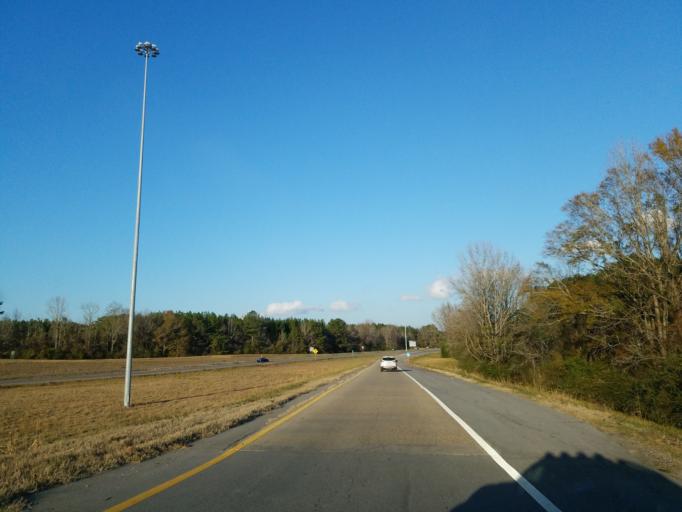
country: US
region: Mississippi
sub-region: Jones County
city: Sharon
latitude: 31.9065
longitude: -89.0145
